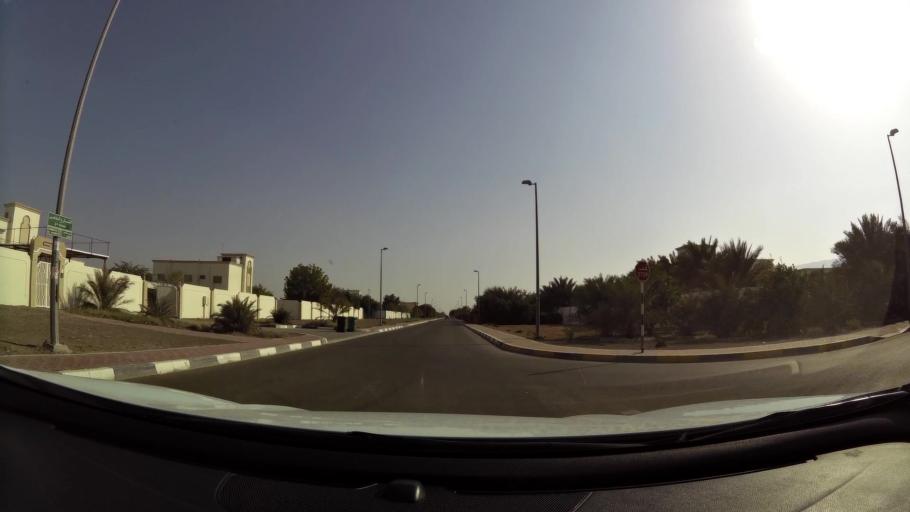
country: AE
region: Abu Dhabi
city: Al Ain
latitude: 24.0843
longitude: 55.8628
